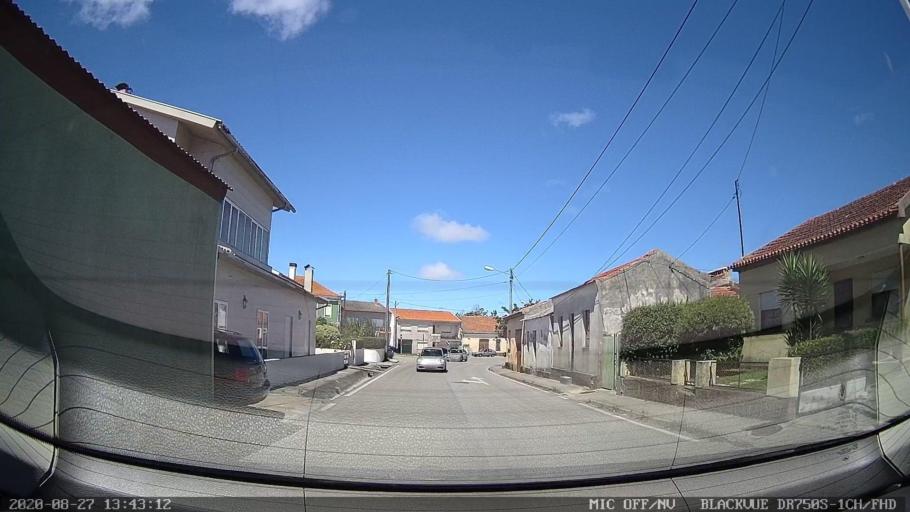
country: PT
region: Coimbra
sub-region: Mira
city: Mira
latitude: 40.4225
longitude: -8.7386
